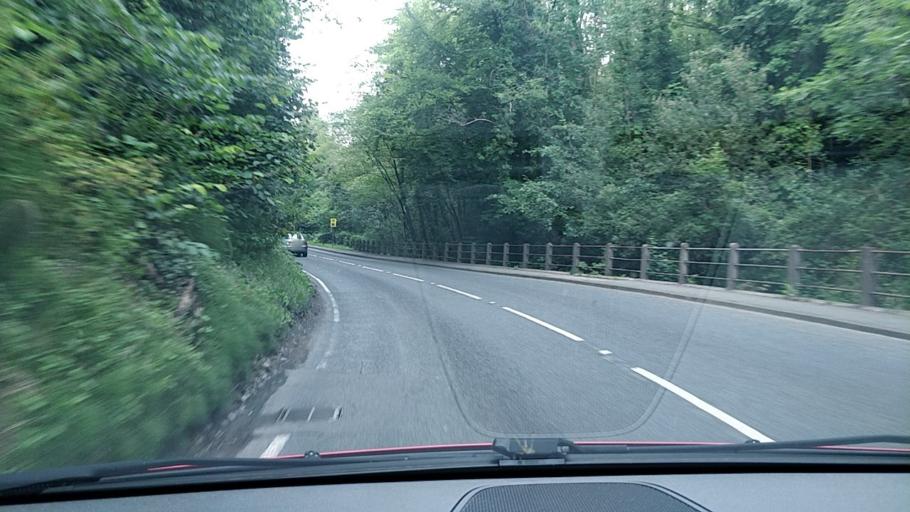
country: GB
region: Wales
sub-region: County of Flintshire
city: Leeswood
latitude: 53.1314
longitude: -3.0828
